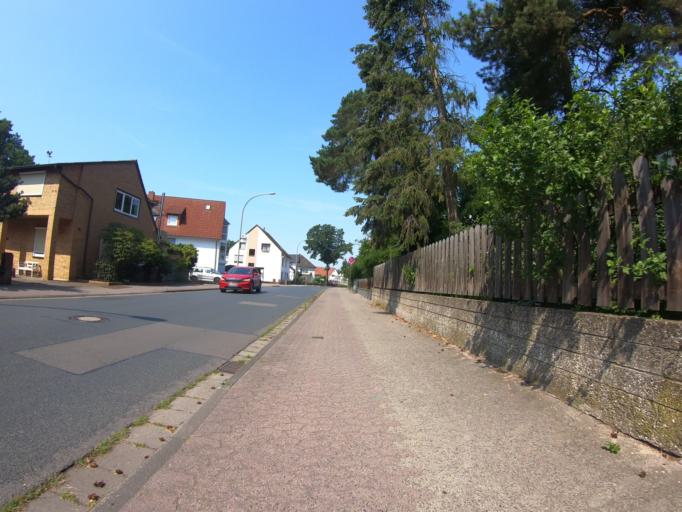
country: DE
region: Lower Saxony
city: Gifhorn
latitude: 52.4790
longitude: 10.5547
